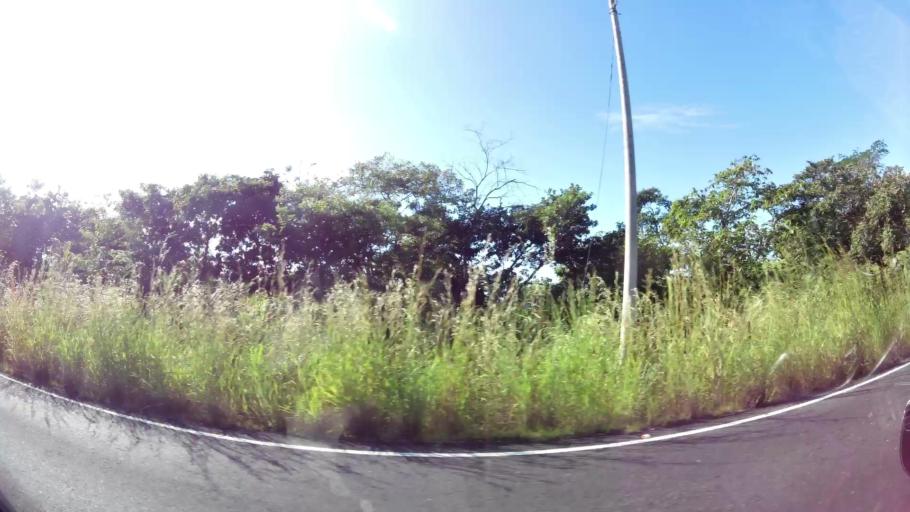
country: CR
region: Guanacaste
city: Sardinal
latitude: 10.5818
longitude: -85.6391
